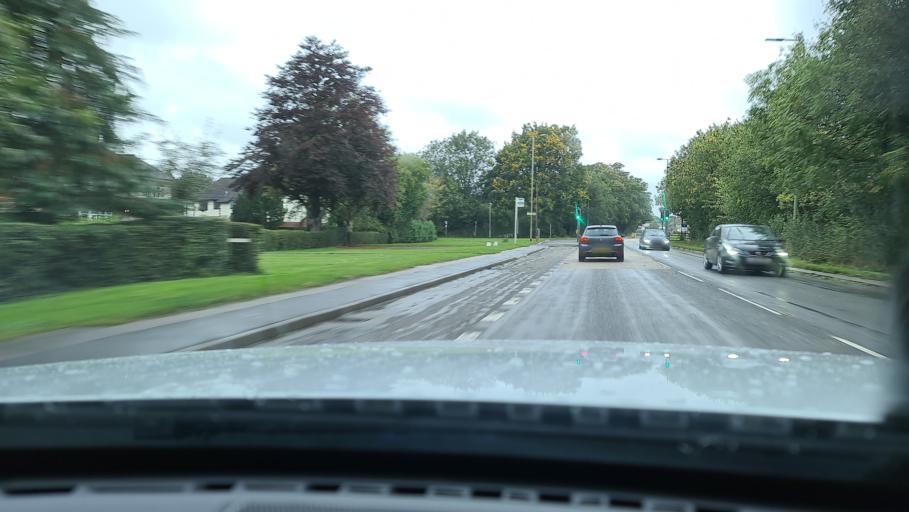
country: GB
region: England
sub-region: Oxfordshire
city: Adderbury
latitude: 52.0388
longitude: -1.3232
